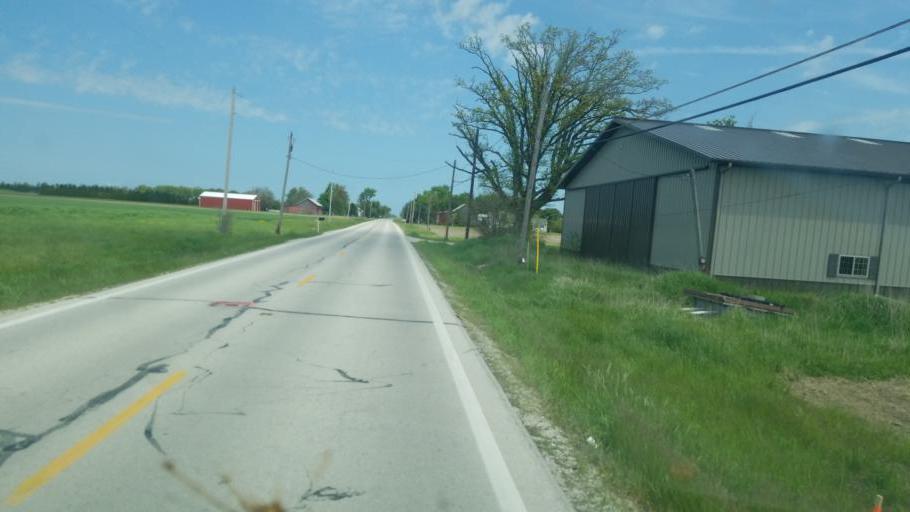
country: US
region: Ohio
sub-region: Ottawa County
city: Oak Harbor
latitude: 41.5597
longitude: -83.1447
